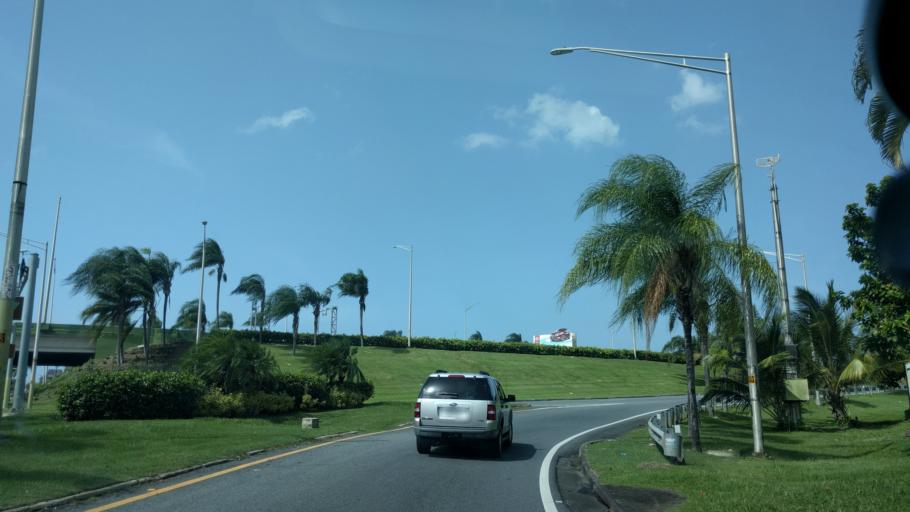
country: PR
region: Toa Baja
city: Sabana Seca
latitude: 18.4199
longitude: -66.1638
